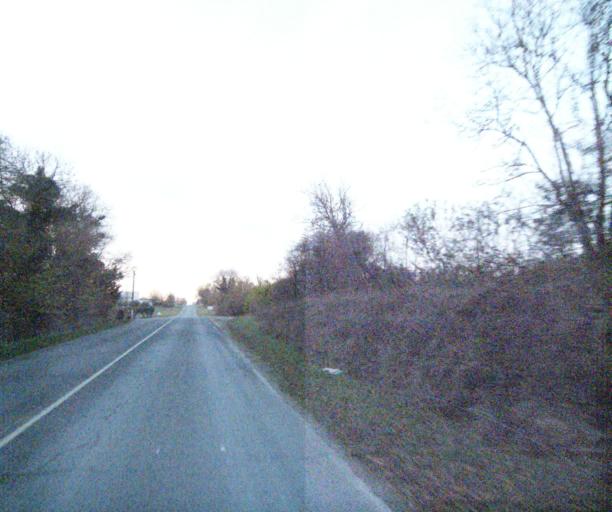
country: FR
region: Poitou-Charentes
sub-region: Departement de la Charente-Maritime
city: Saint-Porchaire
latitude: 45.8155
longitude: -0.7734
